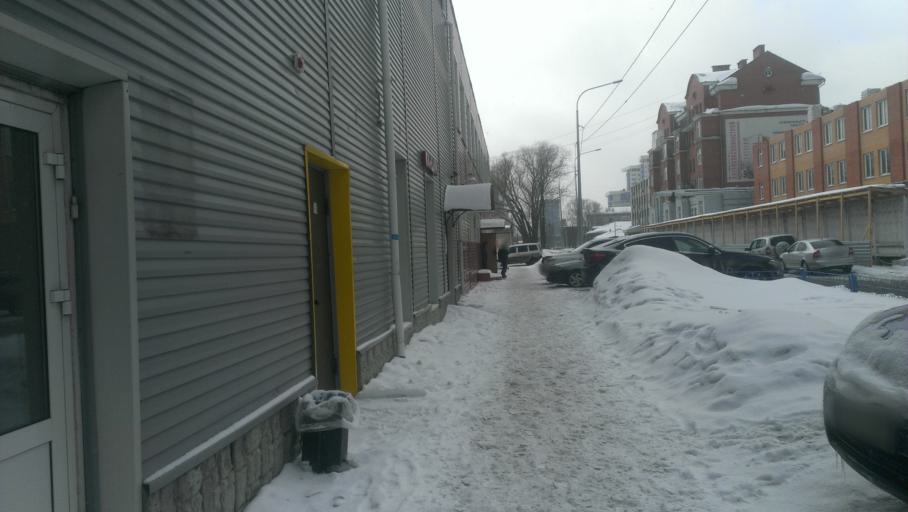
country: RU
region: Altai Krai
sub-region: Gorod Barnaulskiy
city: Barnaul
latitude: 53.3335
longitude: 83.7869
